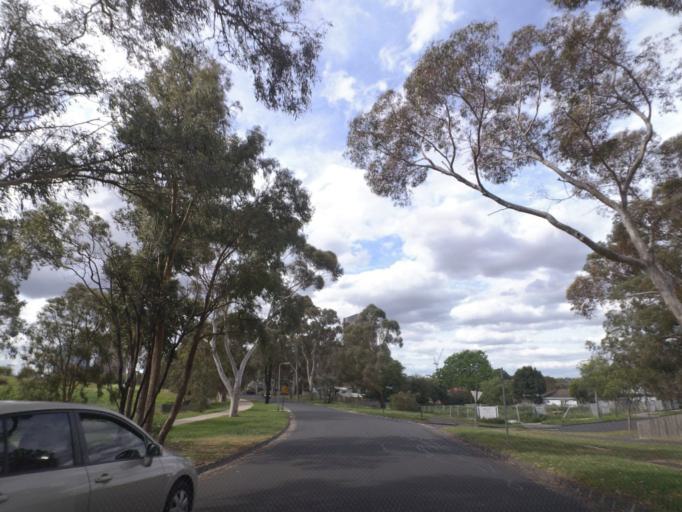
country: AU
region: Victoria
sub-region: Whitehorse
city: Box Hill South
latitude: -37.8246
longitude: 145.1184
